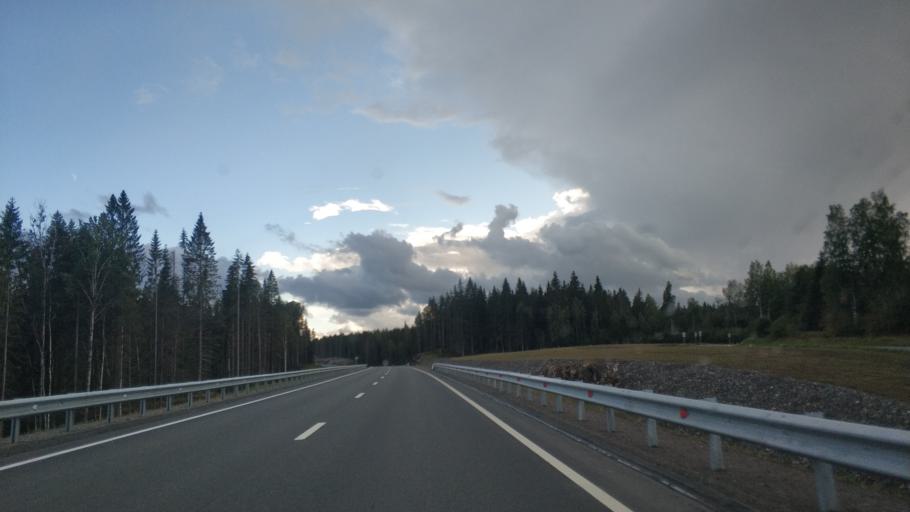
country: RU
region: Republic of Karelia
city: Lakhdenpokh'ya
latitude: 61.4214
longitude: 29.9640
